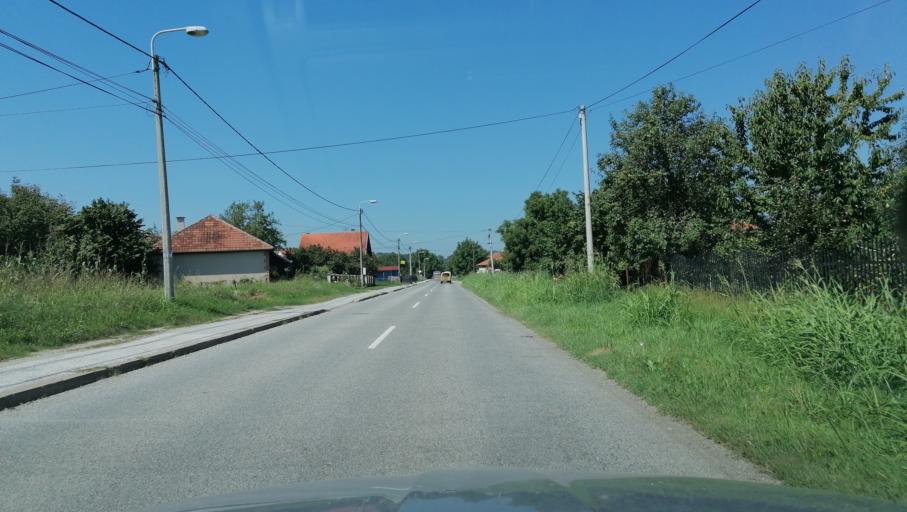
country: RS
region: Central Serbia
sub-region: Raski Okrug
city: Kraljevo
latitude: 43.6899
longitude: 20.6023
